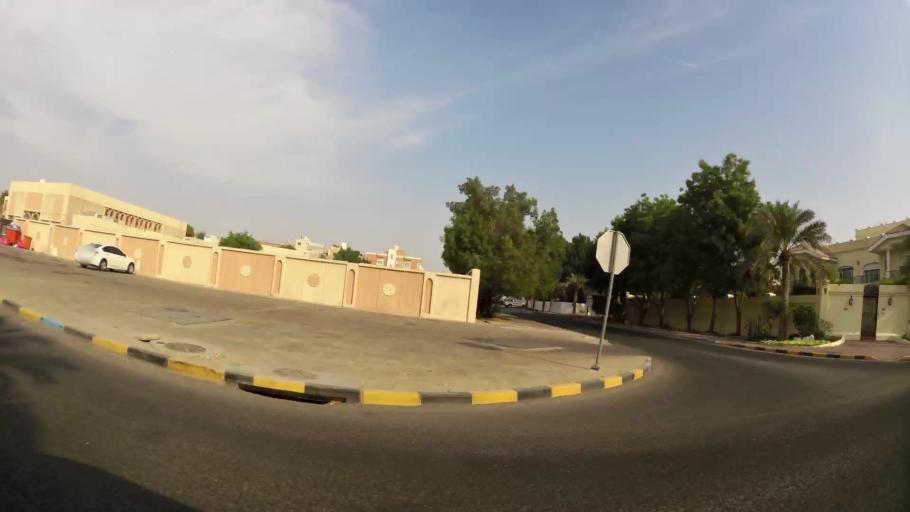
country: KW
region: Al Asimah
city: Ash Shamiyah
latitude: 29.3131
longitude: 47.9887
